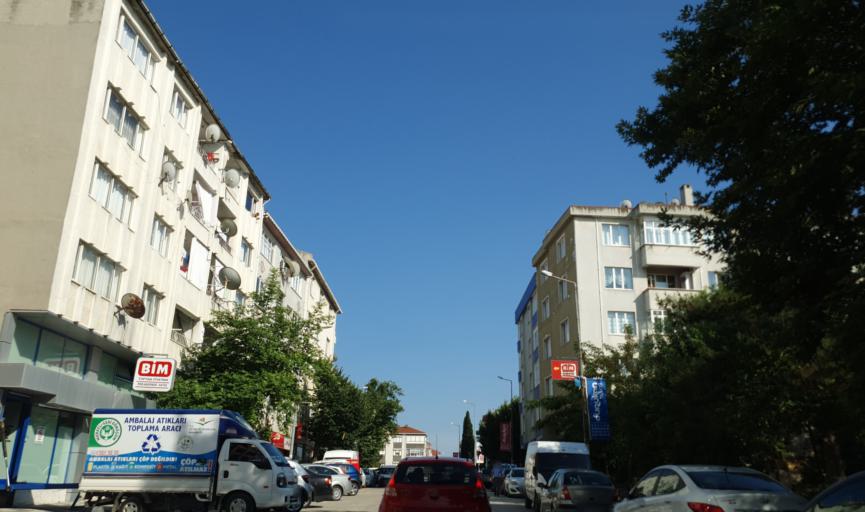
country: TR
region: Tekirdag
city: Saray
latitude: 41.4432
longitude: 27.9192
